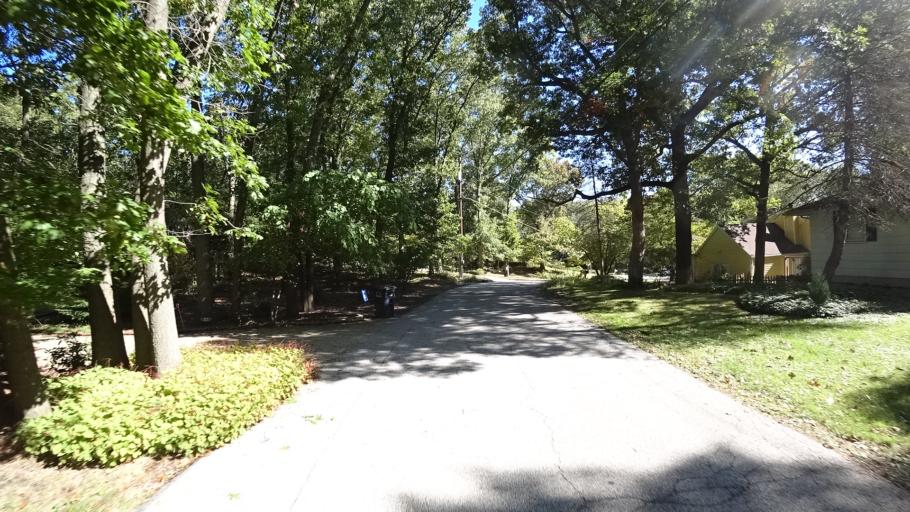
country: US
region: Indiana
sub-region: LaPorte County
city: Long Beach
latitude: 41.7528
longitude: -86.8286
